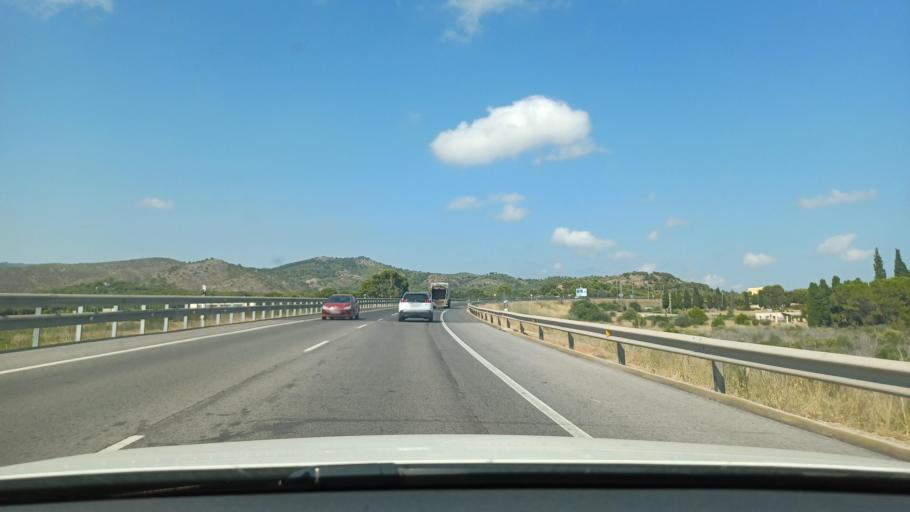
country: ES
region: Valencia
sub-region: Provincia de Castello
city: Borriol
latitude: 39.9999
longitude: -0.0857
